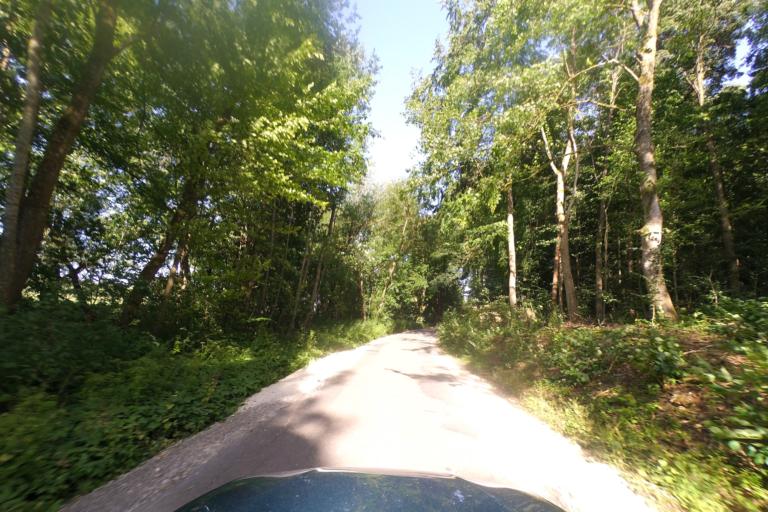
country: DE
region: Baden-Wuerttemberg
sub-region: Regierungsbezirk Stuttgart
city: Hermaringen
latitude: 48.5810
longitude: 10.2426
